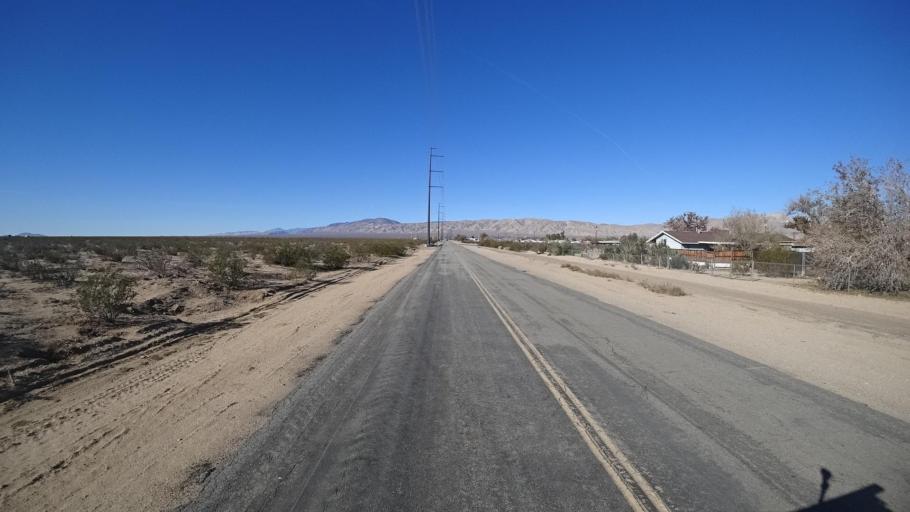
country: US
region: California
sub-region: Kern County
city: California City
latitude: 35.1986
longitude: -118.0136
